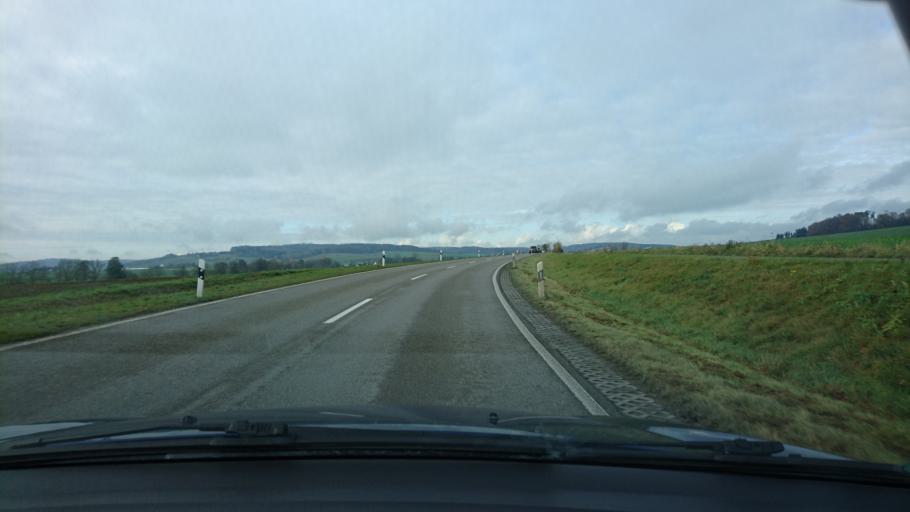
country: DE
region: Bavaria
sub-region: Swabia
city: Tapfheim
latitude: 48.6841
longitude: 10.7049
